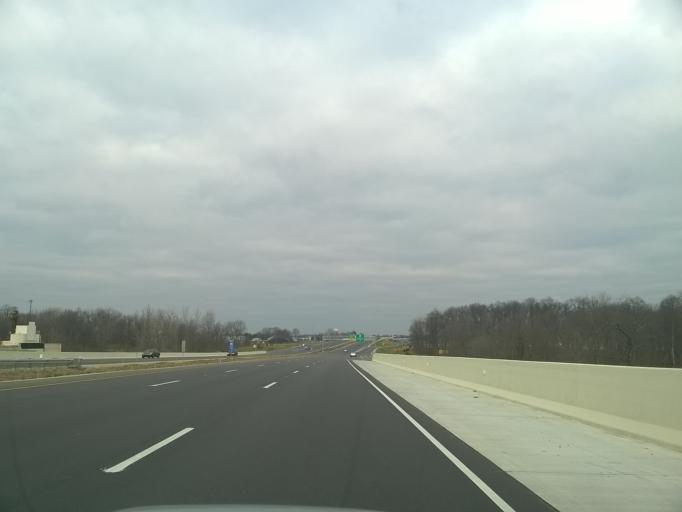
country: US
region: Indiana
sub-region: Hamilton County
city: Westfield
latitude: 40.0346
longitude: -86.1353
